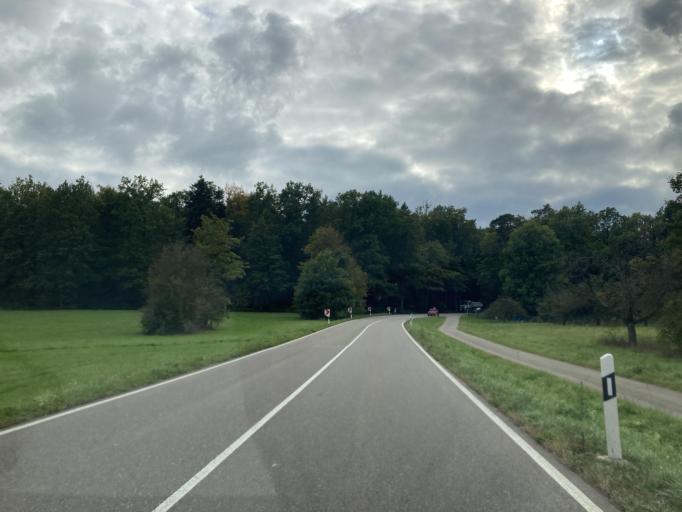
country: DE
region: Baden-Wuerttemberg
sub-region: Karlsruhe Region
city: Birkenfeld
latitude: 48.8672
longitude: 8.6211
